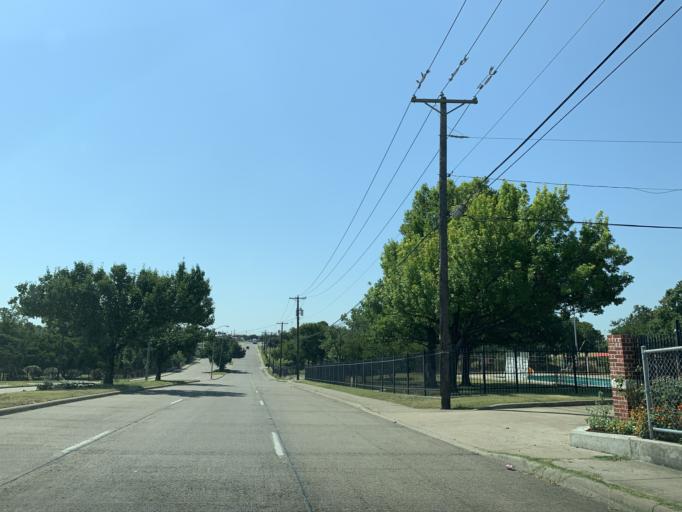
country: US
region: Texas
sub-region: Dallas County
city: Hutchins
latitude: 32.6613
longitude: -96.7533
